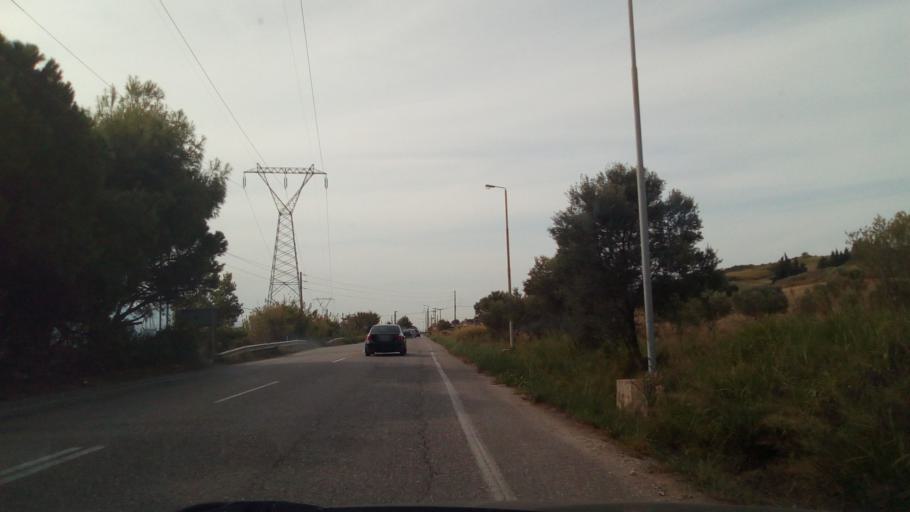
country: GR
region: West Greece
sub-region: Nomos Aitolias kai Akarnanias
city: Antirrio
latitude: 38.3494
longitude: 21.7720
